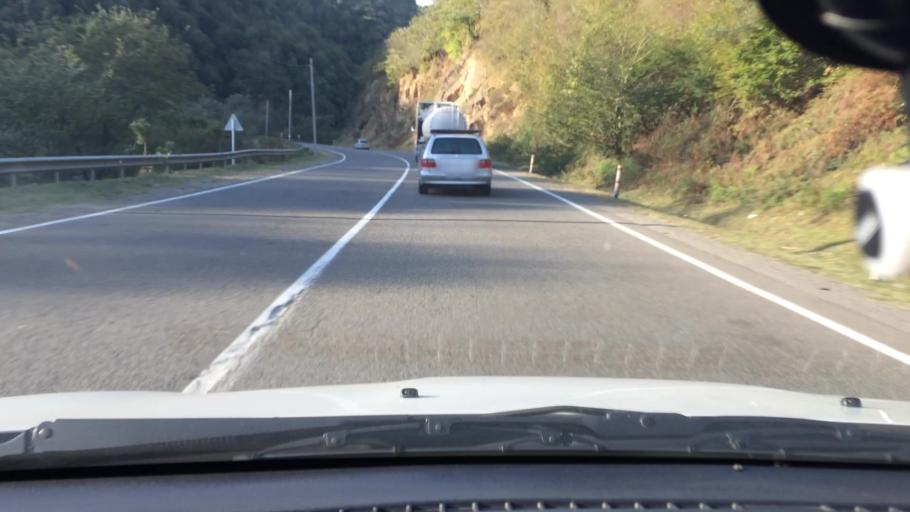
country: GE
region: Imereti
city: Kharagauli
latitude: 42.1074
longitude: 43.2482
